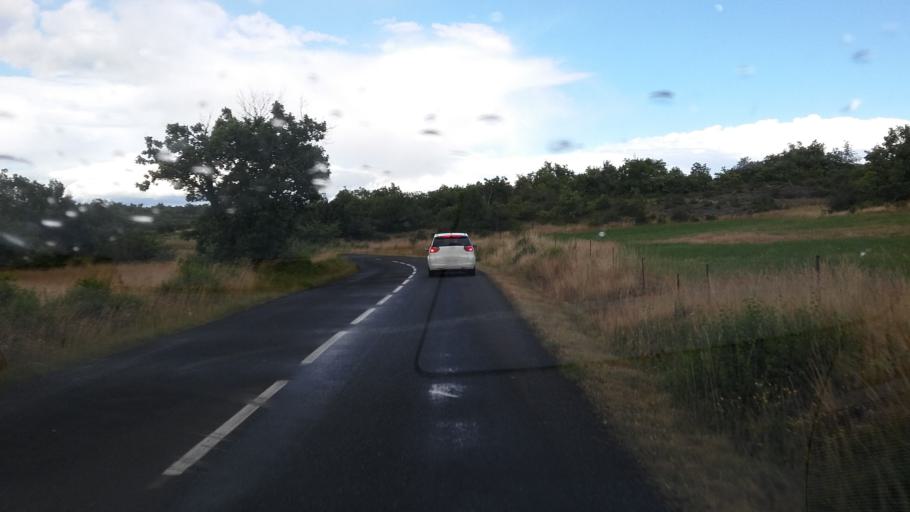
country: FR
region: Midi-Pyrenees
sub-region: Departement de l'Aveyron
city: La Cavalerie
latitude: 43.9520
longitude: 3.2470
